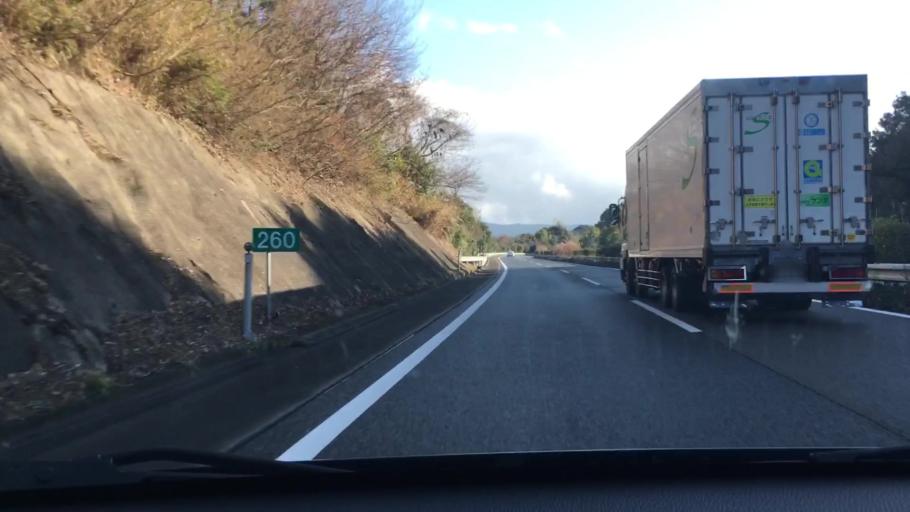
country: JP
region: Kumamoto
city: Hitoyoshi
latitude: 32.1715
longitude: 130.7911
